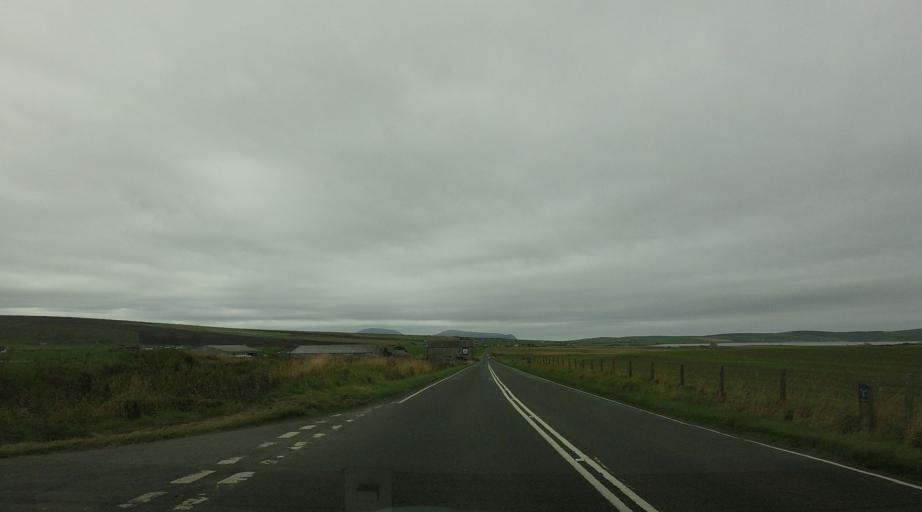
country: GB
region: Scotland
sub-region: Orkney Islands
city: Stromness
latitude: 58.9958
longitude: -3.1838
